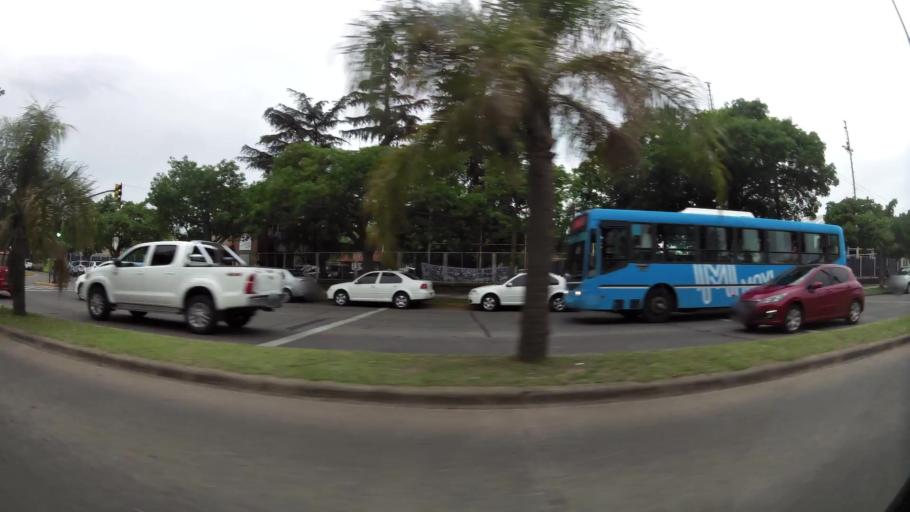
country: AR
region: Santa Fe
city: Granadero Baigorria
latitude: -32.8973
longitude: -60.6844
